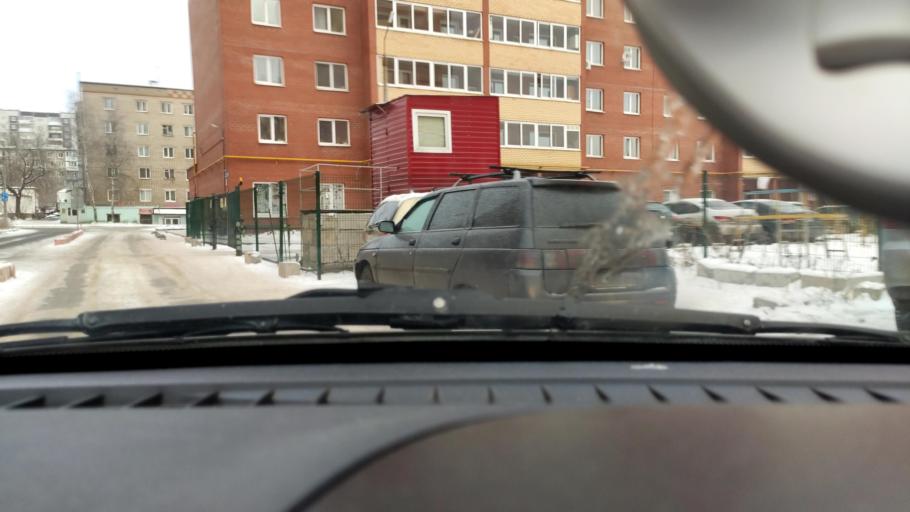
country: RU
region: Perm
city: Perm
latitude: 58.0840
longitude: 56.4046
